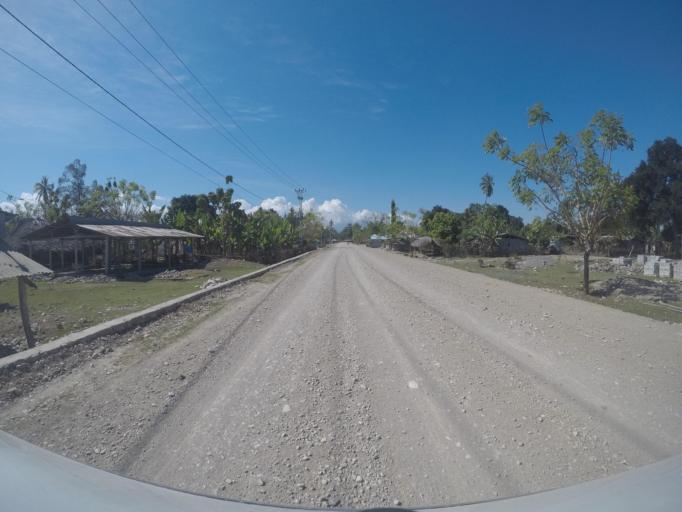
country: TL
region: Viqueque
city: Viqueque
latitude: -8.8654
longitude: 126.5076
